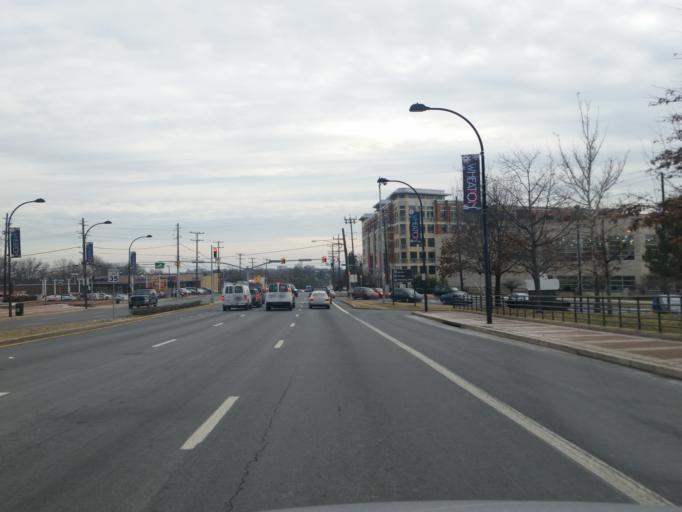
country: US
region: Maryland
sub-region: Montgomery County
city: Wheaton
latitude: 39.0372
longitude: -77.0504
